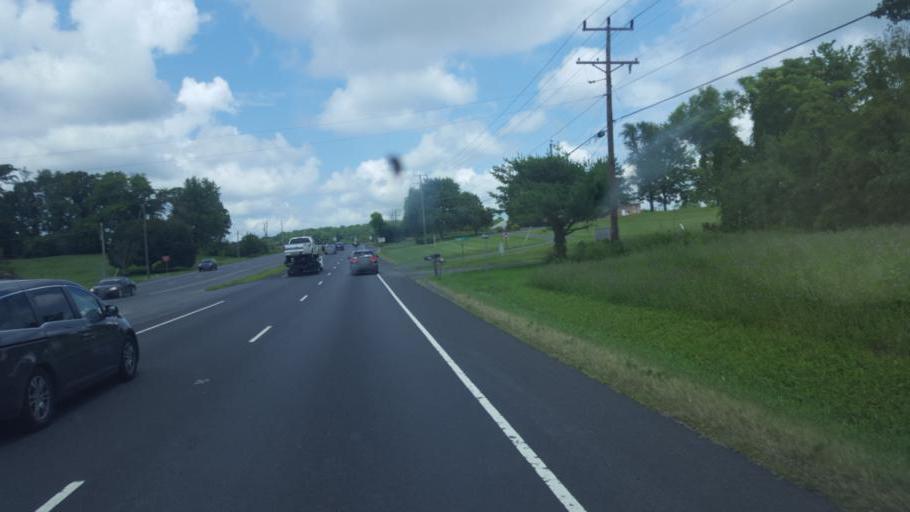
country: US
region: Virginia
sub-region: Fauquier County
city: Warrenton
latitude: 38.6687
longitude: -77.7942
